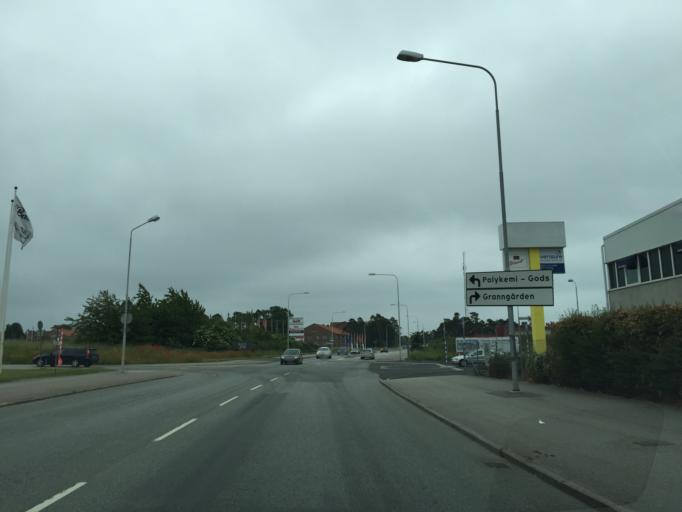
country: SE
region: Skane
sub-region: Ystads Kommun
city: Ystad
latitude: 55.4358
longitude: 13.8376
